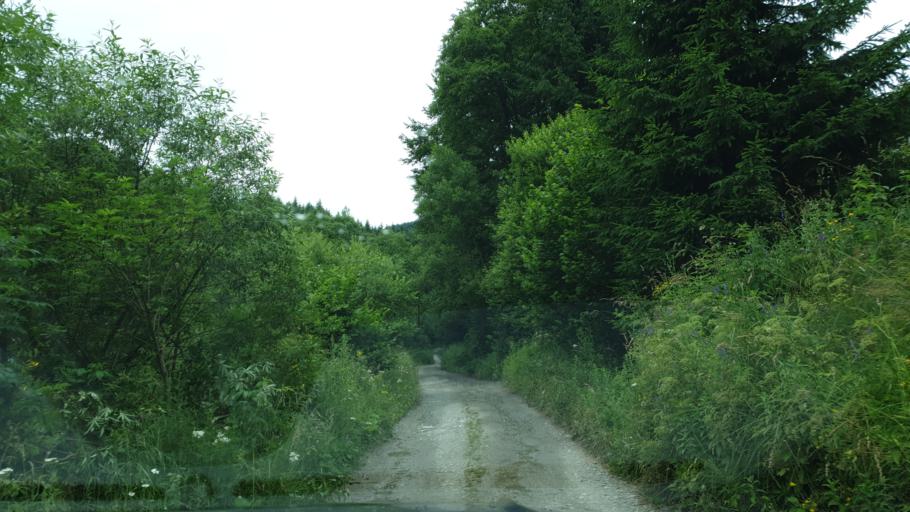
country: RO
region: Hunedoara
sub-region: Comuna Uricani
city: Uricani
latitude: 45.3017
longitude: 22.9906
